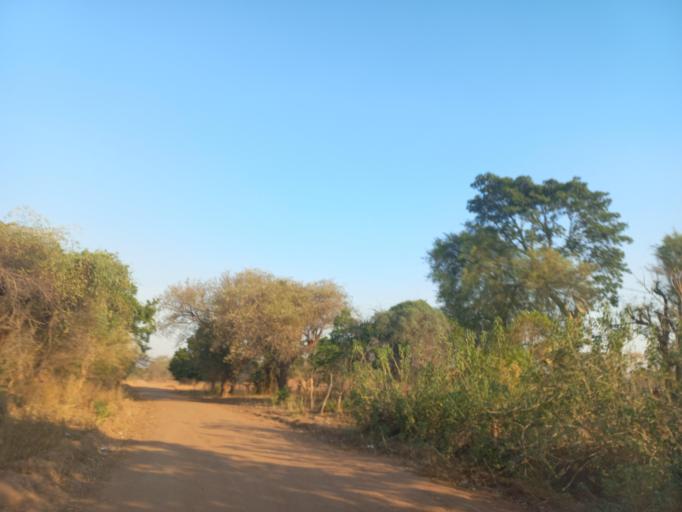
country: ZM
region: Lusaka
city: Luangwa
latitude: -15.4339
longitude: 30.3459
